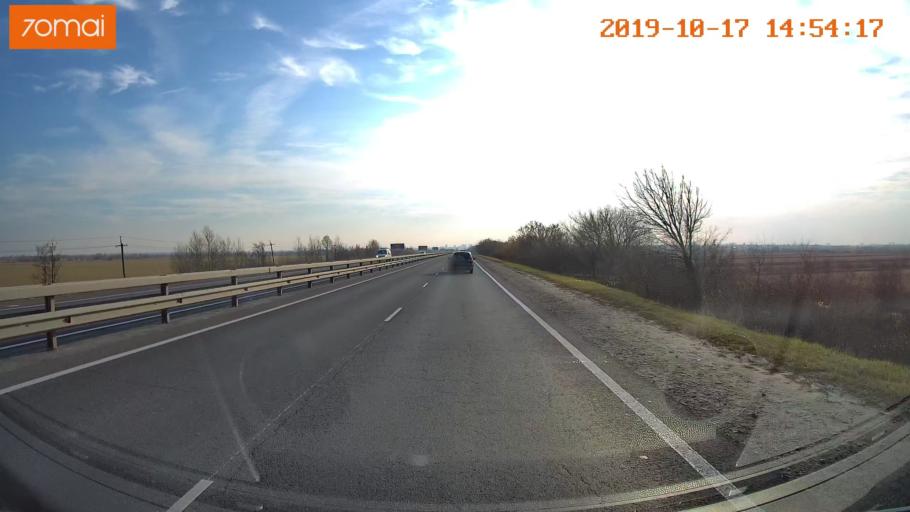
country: RU
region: Rjazan
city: Polyany
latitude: 54.6835
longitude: 39.8330
